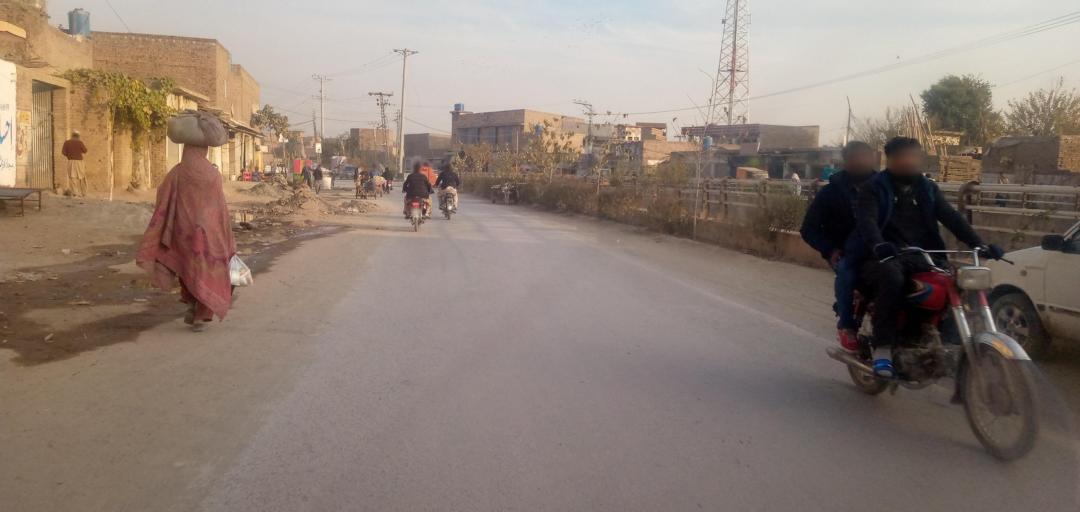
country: PK
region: Khyber Pakhtunkhwa
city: Peshawar
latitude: 33.9730
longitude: 71.5206
